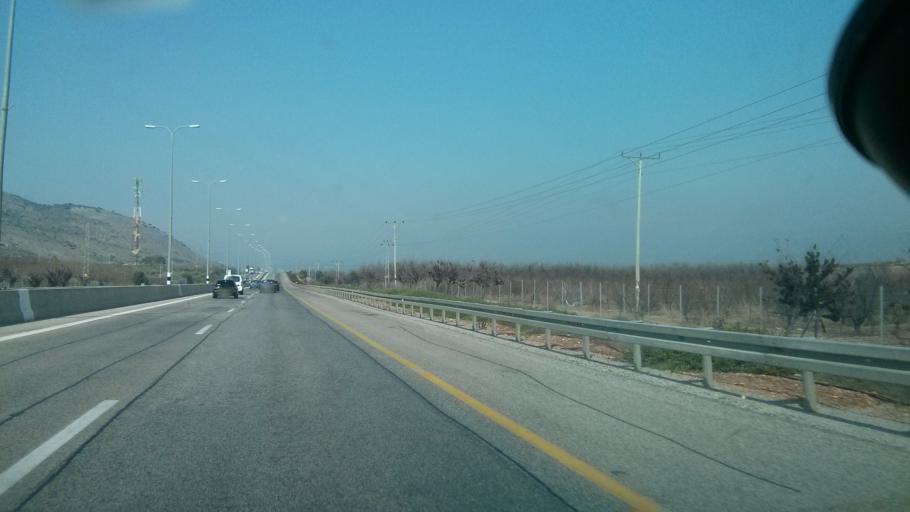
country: IL
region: Northern District
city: Rosh Pinna
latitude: 33.0509
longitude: 35.5728
